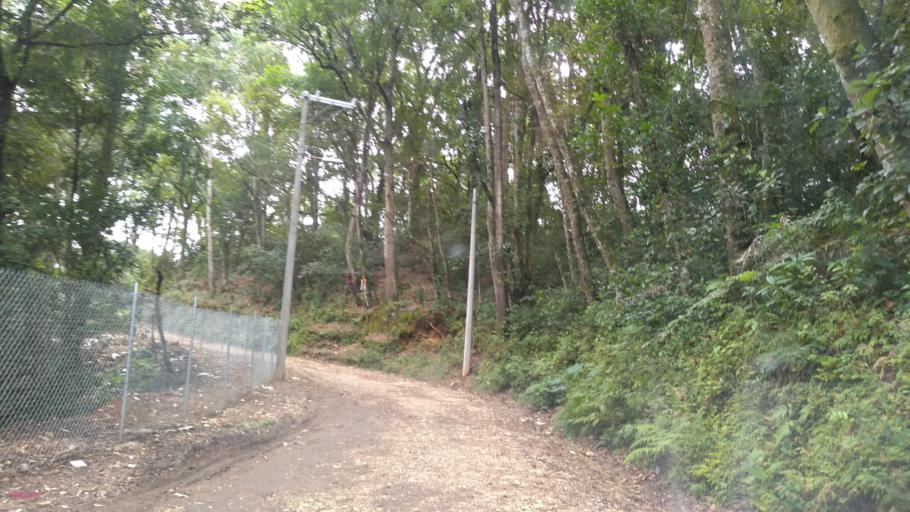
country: MX
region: Veracruz
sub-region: Tlalnelhuayocan
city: Guadalupe Victoria
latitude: 19.5406
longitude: -96.9692
